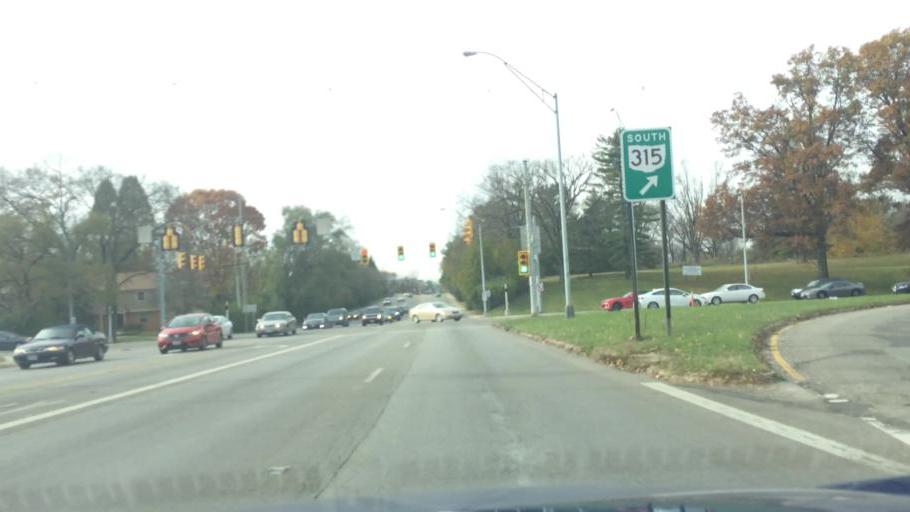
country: US
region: Ohio
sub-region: Franklin County
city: Worthington
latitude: 40.0520
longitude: -83.0331
